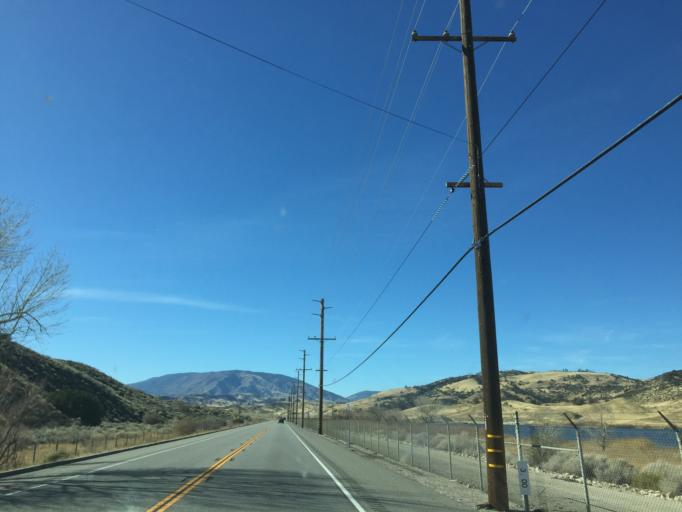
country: US
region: California
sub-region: Kern County
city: Lebec
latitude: 34.7694
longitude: -118.7498
